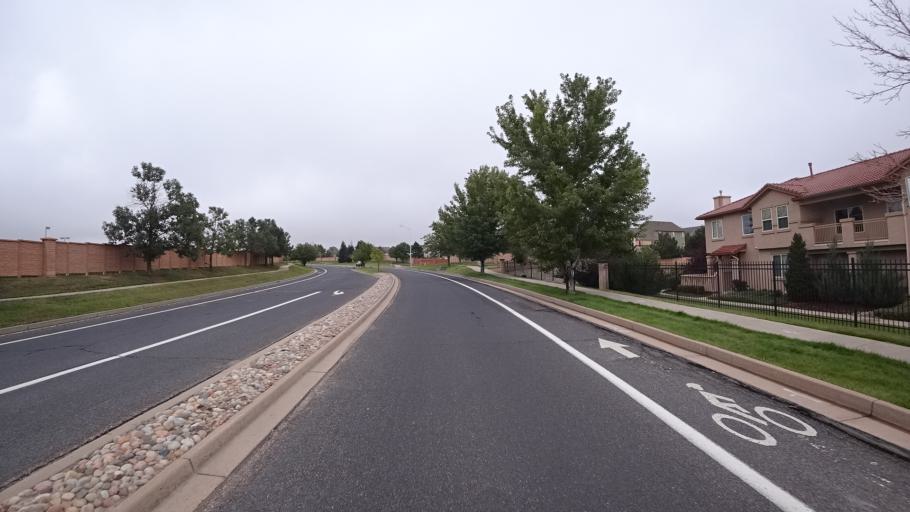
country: US
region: Colorado
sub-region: El Paso County
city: Black Forest
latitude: 38.9354
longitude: -104.7385
